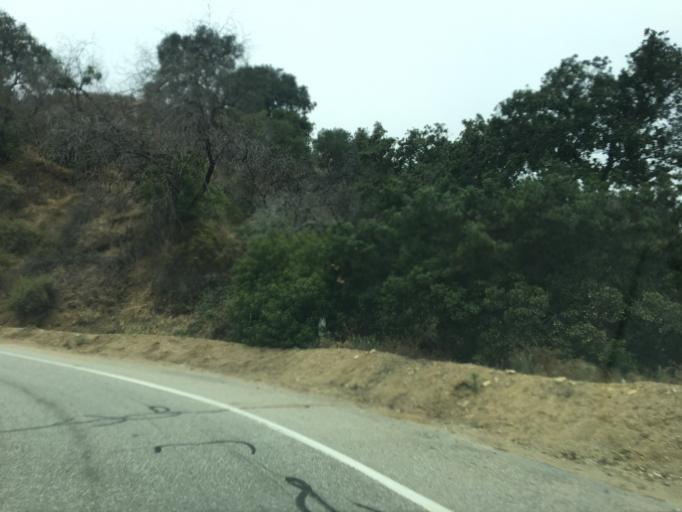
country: US
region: California
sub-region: Los Angeles County
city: Glendora
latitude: 34.1626
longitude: -117.8434
